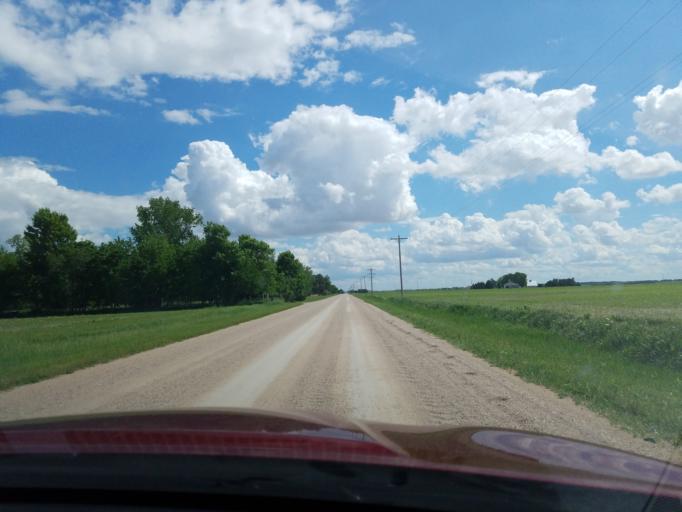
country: US
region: Nebraska
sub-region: Buffalo County
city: Kearney
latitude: 40.6458
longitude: -99.0086
